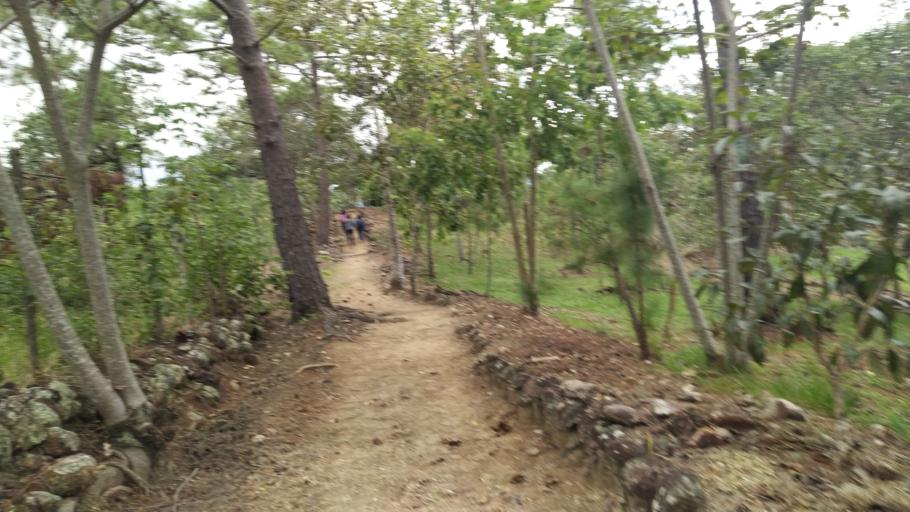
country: GT
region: Chiquimula
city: Esquipulas
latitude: 14.5556
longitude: -89.3199
